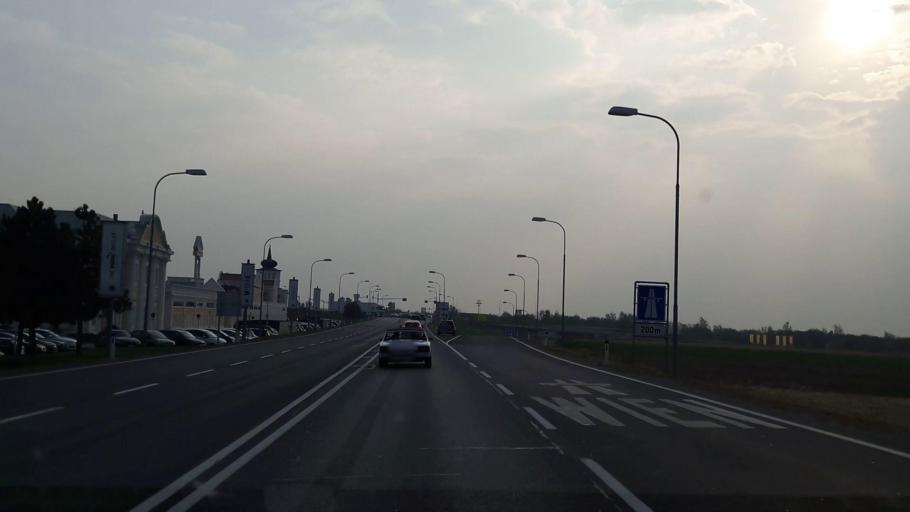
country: AT
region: Burgenland
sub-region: Politischer Bezirk Neusiedl am See
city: Parndorf
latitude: 47.9808
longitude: 16.8468
